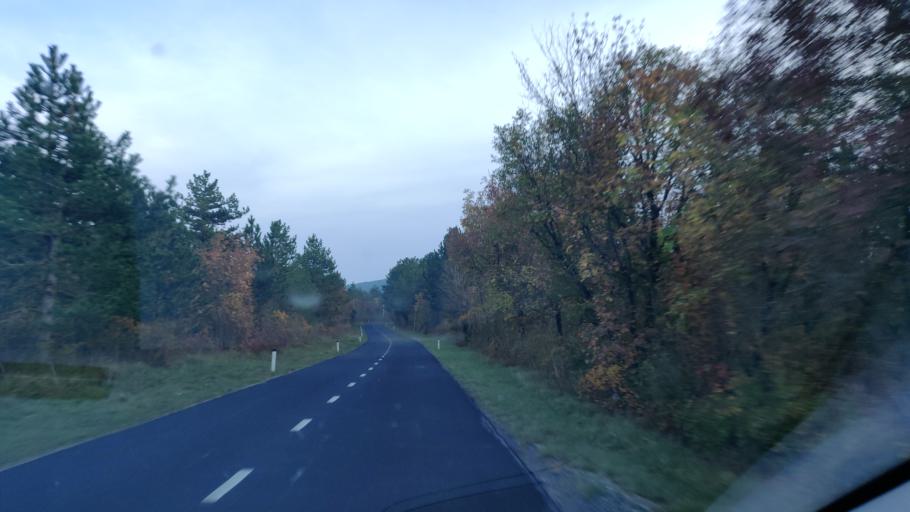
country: SI
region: Sezana
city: Sezana
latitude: 45.7491
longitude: 13.9242
